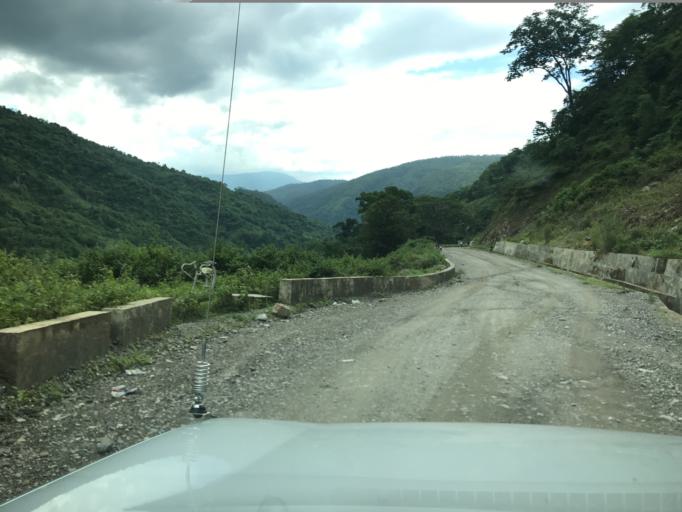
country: TL
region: Aileu
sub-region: Aileu Villa
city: Aileu
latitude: -8.6440
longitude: 125.5210
